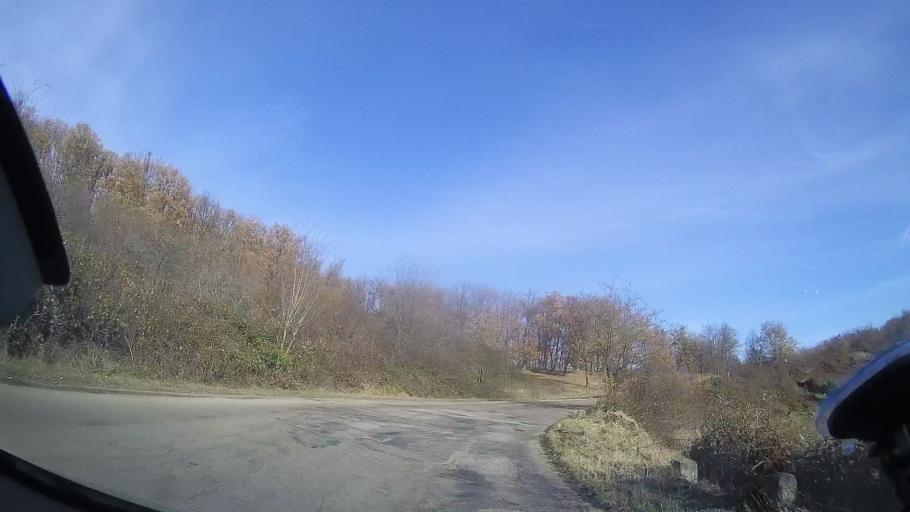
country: RO
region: Bihor
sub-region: Comuna Brusturi
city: Brusturi
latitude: 47.1018
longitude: 22.2441
